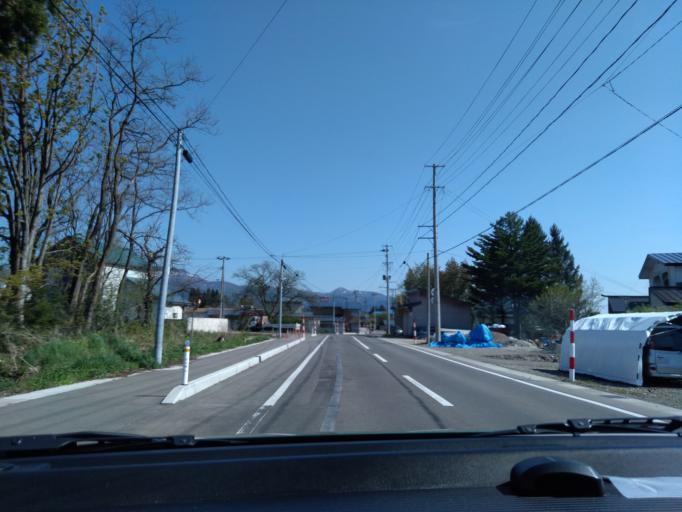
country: JP
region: Akita
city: Kakunodatemachi
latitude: 39.5113
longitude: 140.5932
